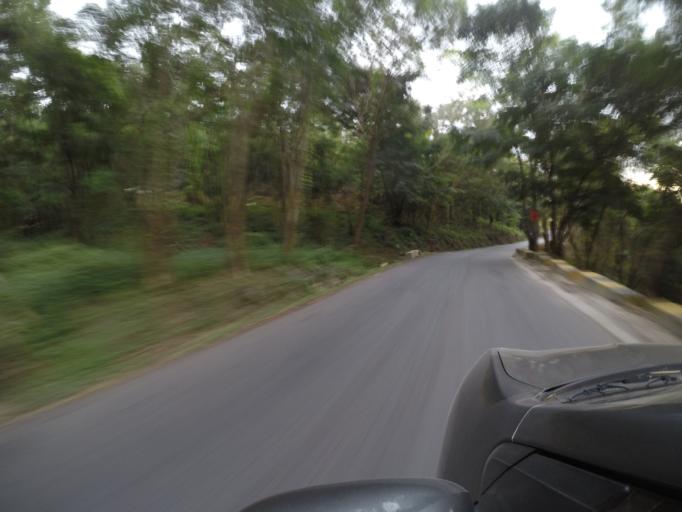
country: MM
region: Shan
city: Taunggyi
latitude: 20.8099
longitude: 97.0254
